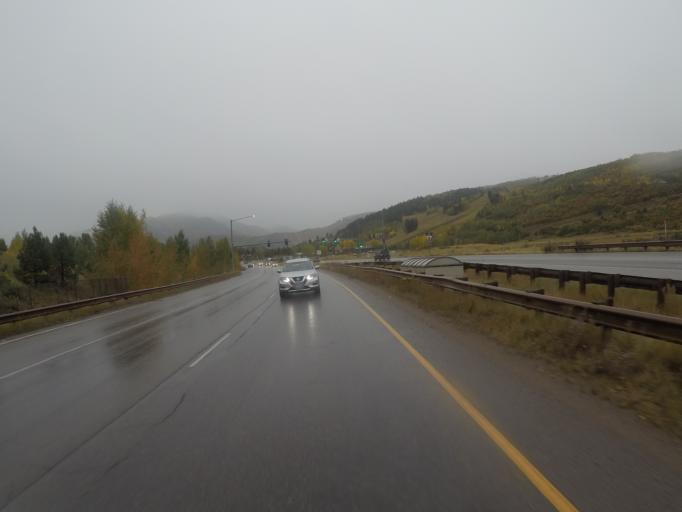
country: US
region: Colorado
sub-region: Pitkin County
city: Aspen
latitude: 39.2103
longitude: -106.8615
